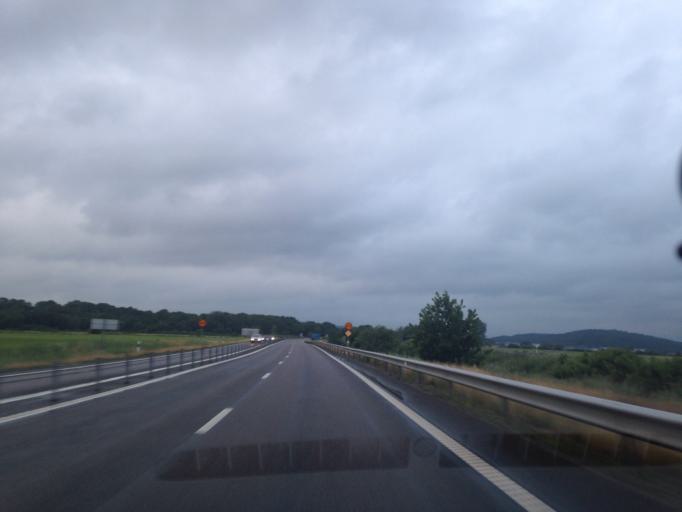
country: SE
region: Halland
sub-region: Varbergs Kommun
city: Varberg
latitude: 57.1473
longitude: 12.2689
